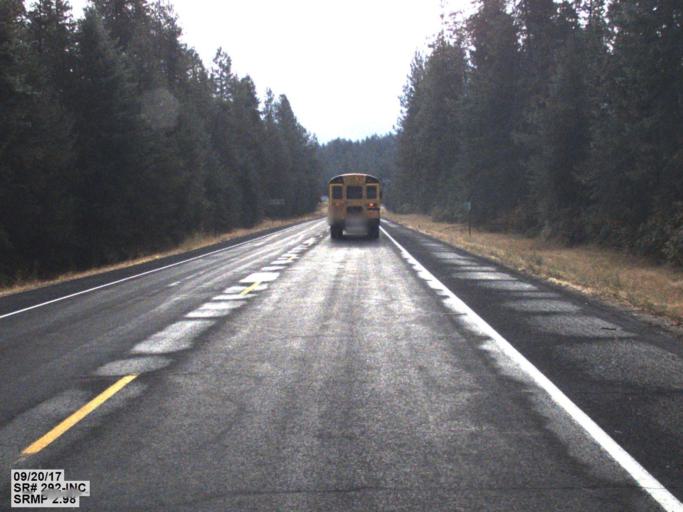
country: US
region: Washington
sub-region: Stevens County
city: Chewelah
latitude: 48.0638
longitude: -117.6810
